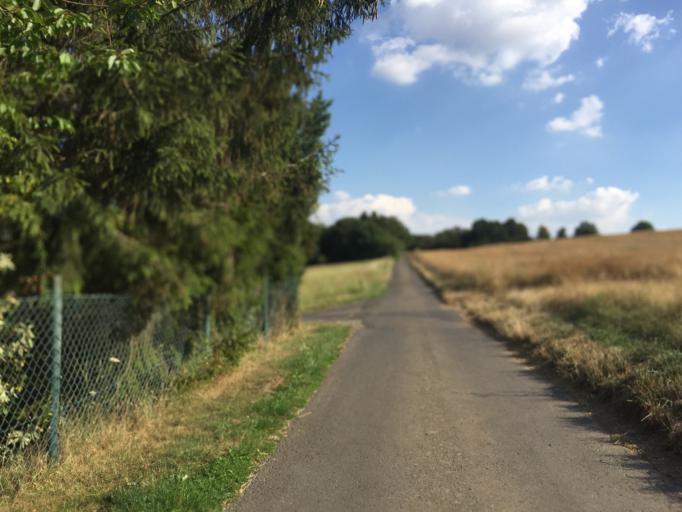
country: DE
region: Hesse
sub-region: Regierungsbezirk Giessen
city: Langgons
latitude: 50.5274
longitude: 8.7077
